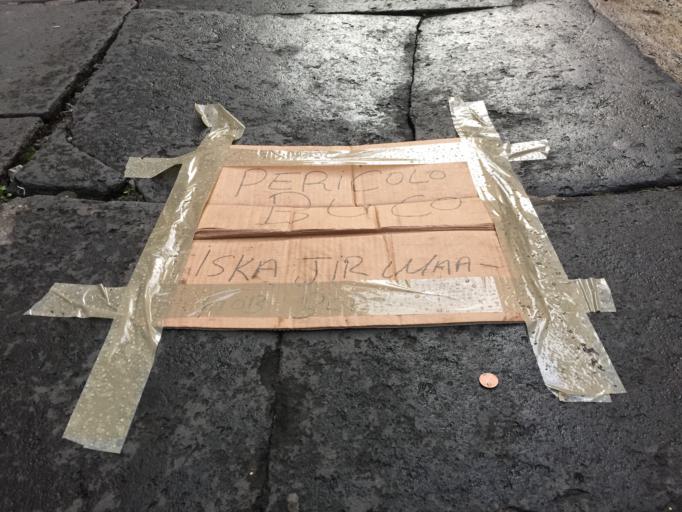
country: IT
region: Latium
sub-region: Citta metropolitana di Roma Capitale
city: Rome
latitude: 41.9022
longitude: 12.5041
